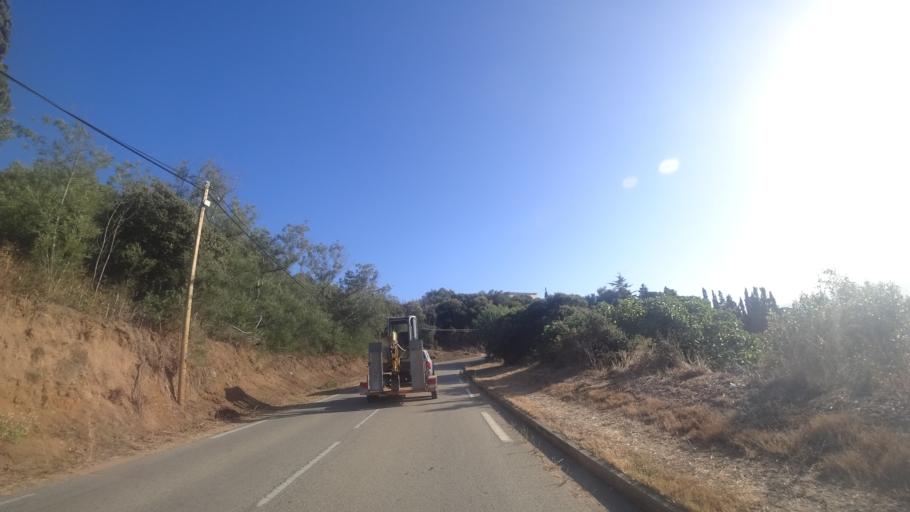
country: FR
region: Corsica
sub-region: Departement de la Corse-du-Sud
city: Cargese
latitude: 42.1406
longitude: 8.6016
